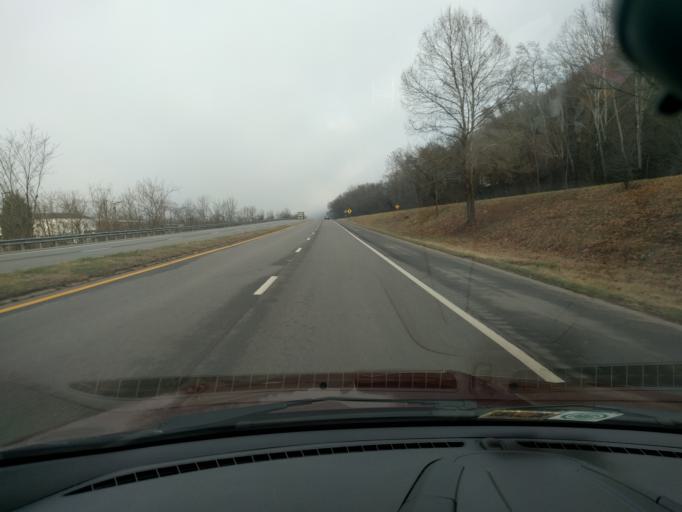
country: US
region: West Virginia
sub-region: Kanawha County
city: Chesapeake
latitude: 38.2258
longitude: -81.5297
